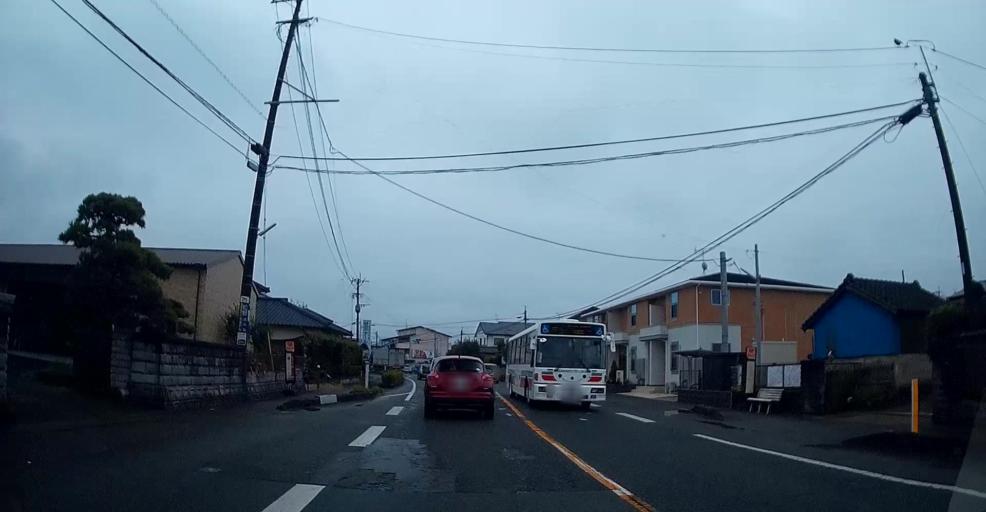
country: JP
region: Kumamoto
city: Kumamoto
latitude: 32.7449
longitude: 130.7393
